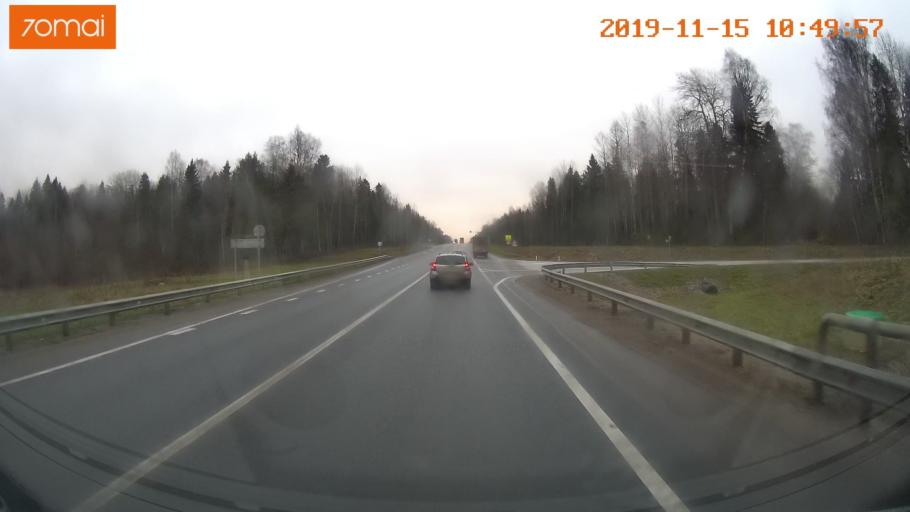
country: RU
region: Vologda
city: Sheksna
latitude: 59.1876
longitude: 38.6709
